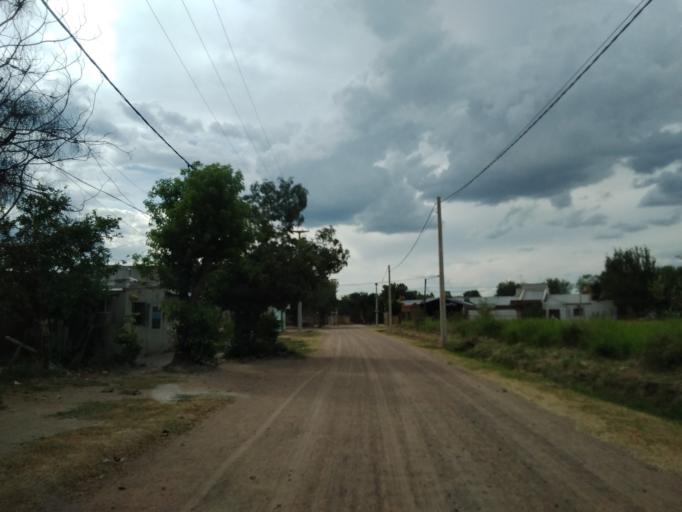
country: AR
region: Corrientes
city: Corrientes
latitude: -27.5233
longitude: -58.7946
